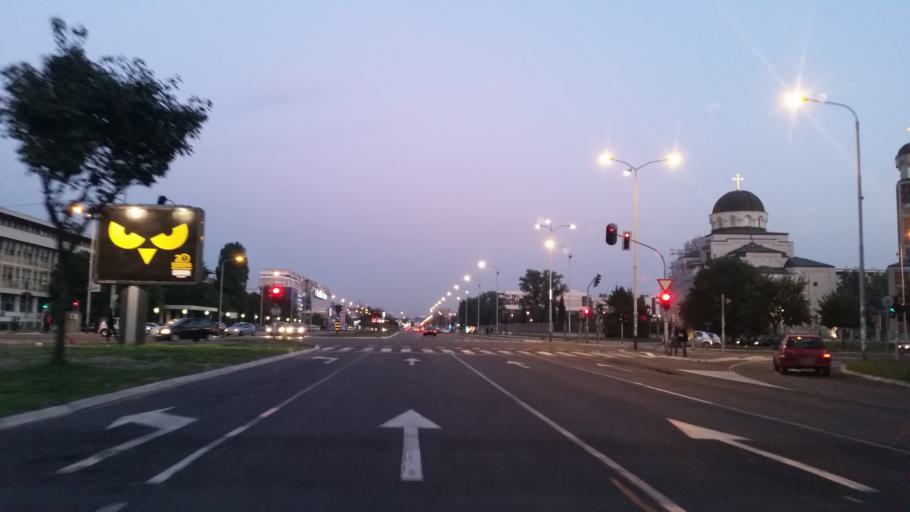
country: RS
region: Central Serbia
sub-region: Belgrade
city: Novi Beograd
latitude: 44.8214
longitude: 20.4097
